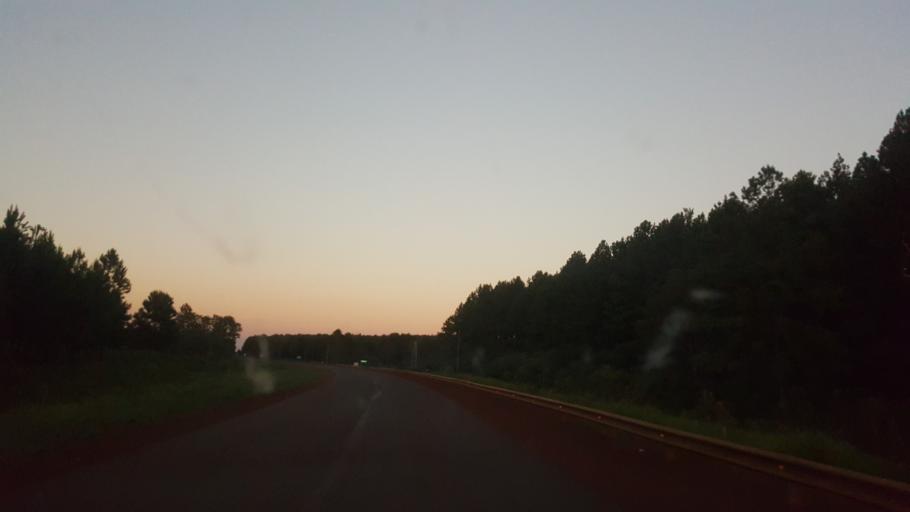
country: AR
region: Corrientes
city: Garruchos
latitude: -28.2269
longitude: -55.8013
